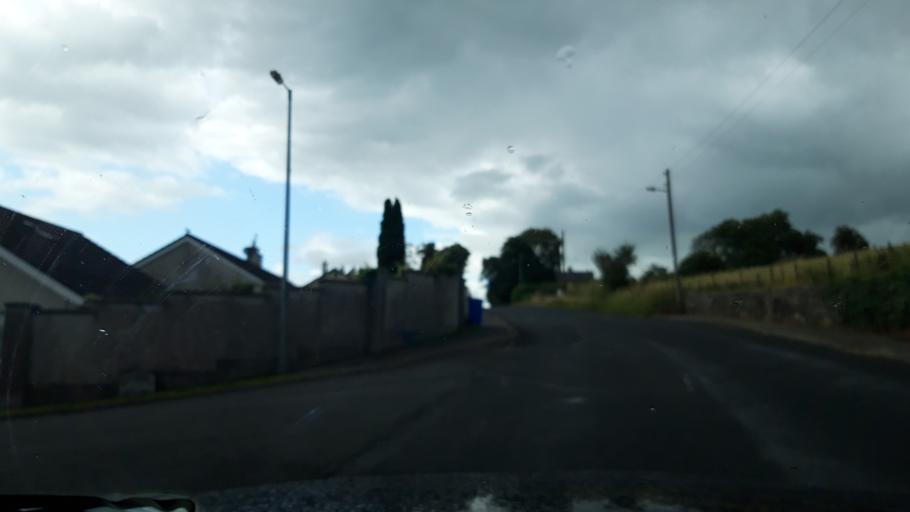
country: IE
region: Leinster
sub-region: Wicklow
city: Baltinglass
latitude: 52.9428
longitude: -6.7052
